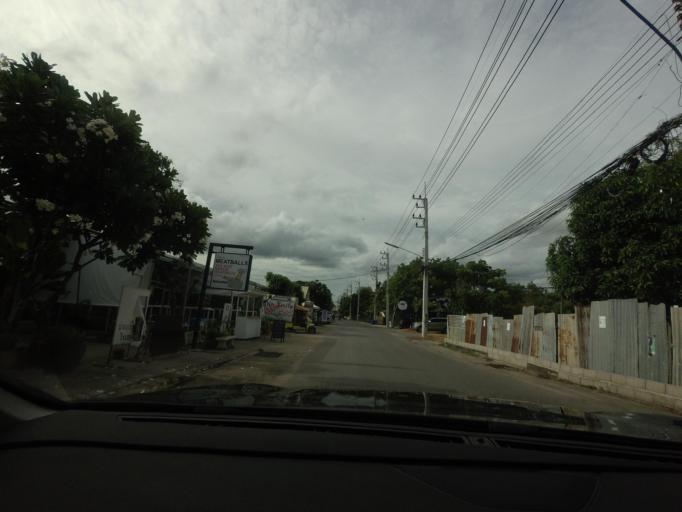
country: TH
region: Prachuap Khiri Khan
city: Hua Hin
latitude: 12.5555
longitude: 99.9552
